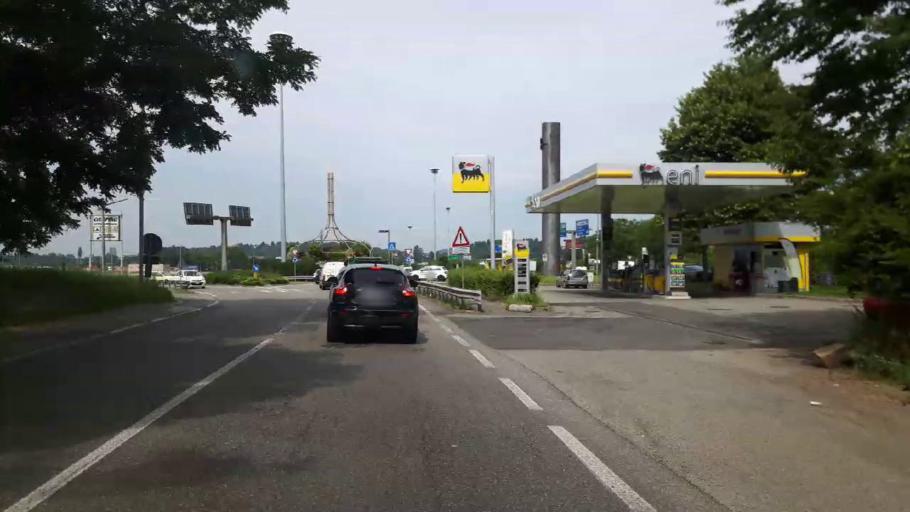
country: IT
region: Lombardy
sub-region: Provincia di Como
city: Lucino
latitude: 45.7839
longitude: 9.0606
